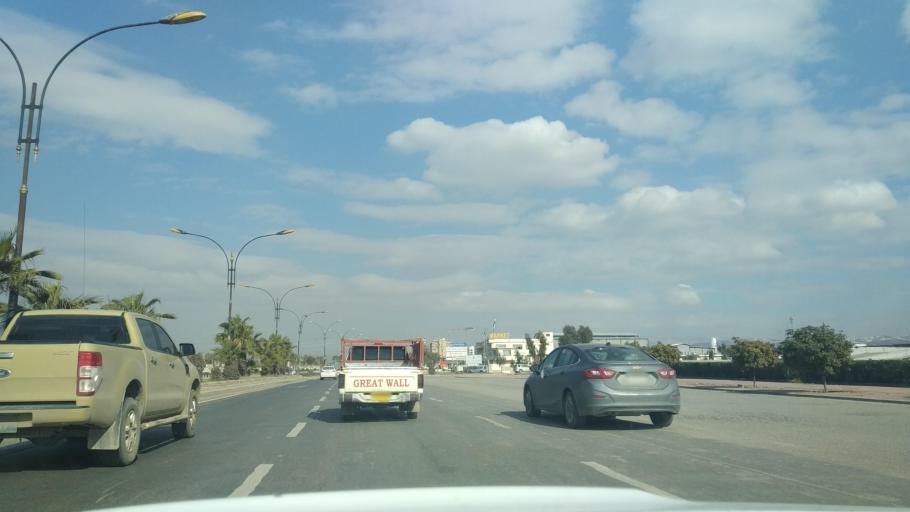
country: IQ
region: Arbil
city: Erbil
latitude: 36.2546
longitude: 44.0807
